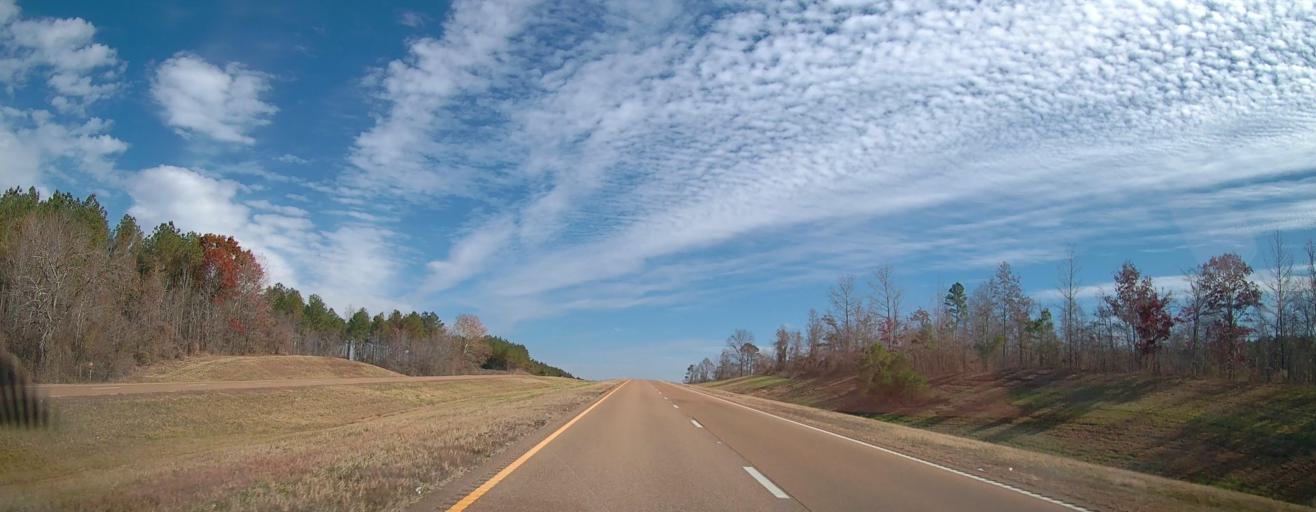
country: US
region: Mississippi
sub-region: Benton County
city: Ashland
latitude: 34.9488
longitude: -89.1020
